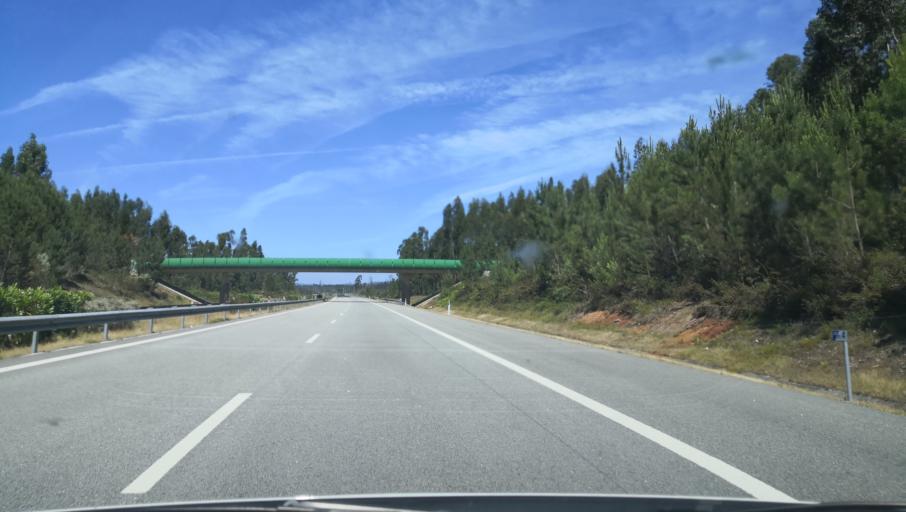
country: PT
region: Coimbra
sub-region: Montemor-O-Velho
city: Arazede
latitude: 40.2768
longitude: -8.5909
